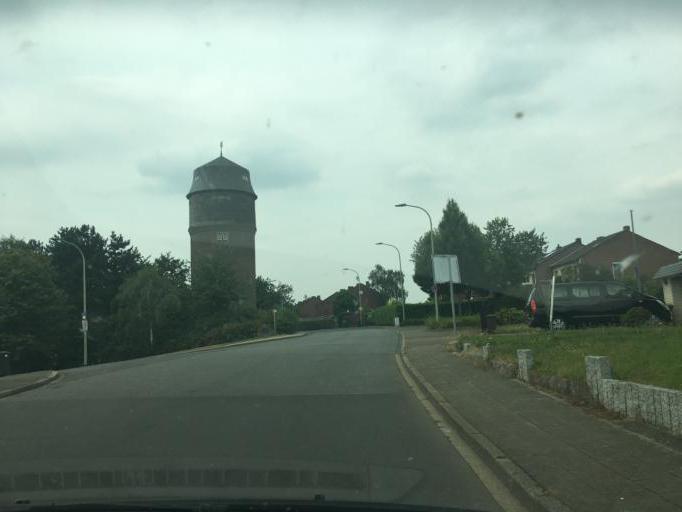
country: DE
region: North Rhine-Westphalia
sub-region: Regierungsbezirk Koln
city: Merzenich
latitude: 50.8228
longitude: 6.5350
